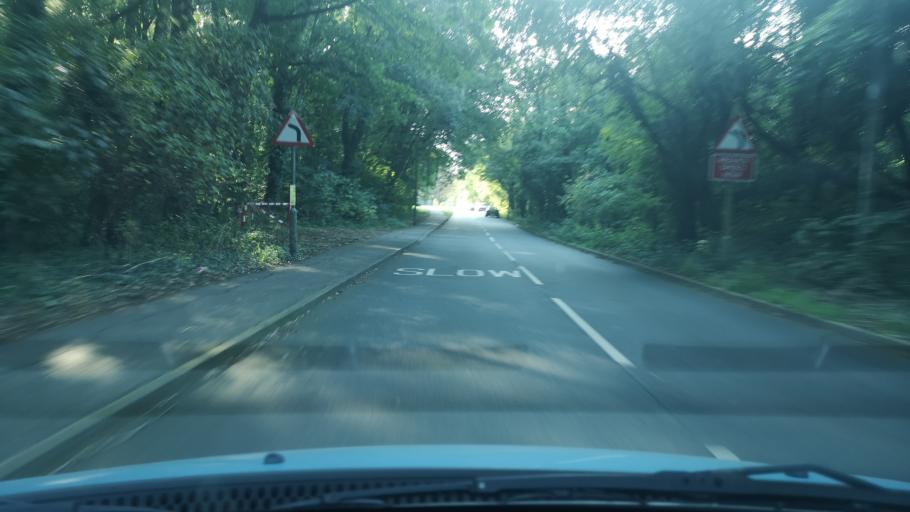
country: GB
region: England
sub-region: North Lincolnshire
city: Scunthorpe
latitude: 53.5845
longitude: -0.6686
